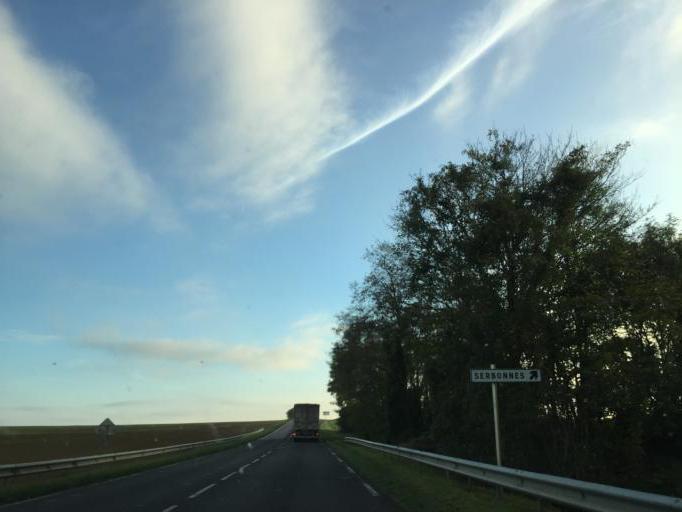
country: FR
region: Bourgogne
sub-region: Departement de l'Yonne
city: Sergines
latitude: 48.3409
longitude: 3.2311
